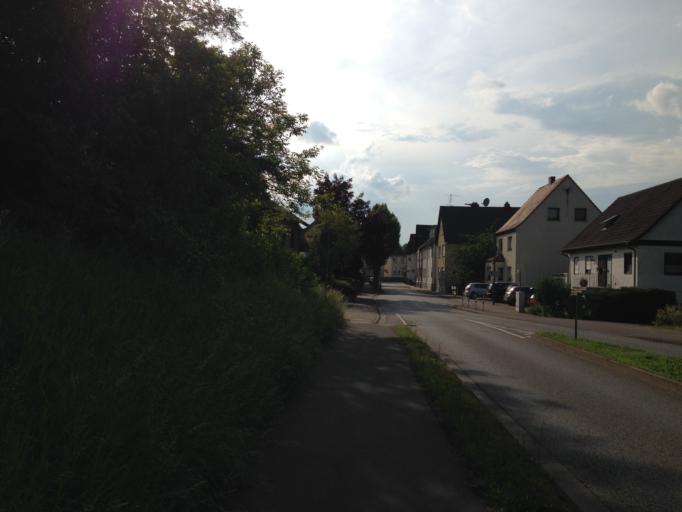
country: DE
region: Hesse
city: Allendorf an der Lahn
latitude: 50.5477
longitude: 8.6210
